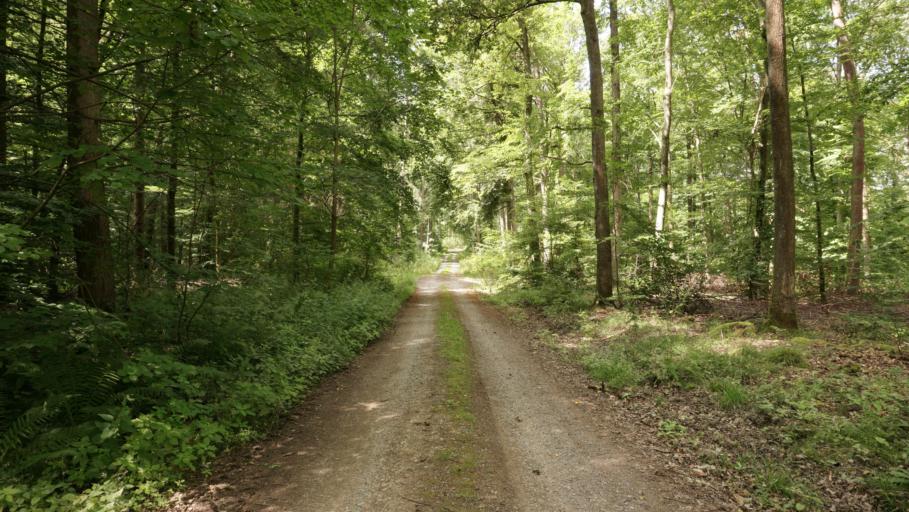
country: DE
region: Baden-Wuerttemberg
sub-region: Karlsruhe Region
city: Hassmersheim
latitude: 49.3210
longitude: 9.1961
